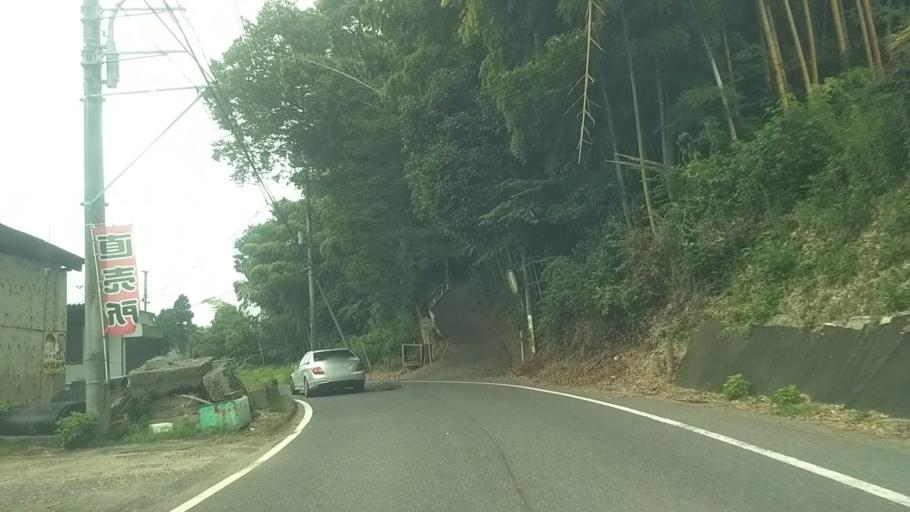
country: JP
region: Chiba
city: Futtsu
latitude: 35.2187
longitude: 139.8771
